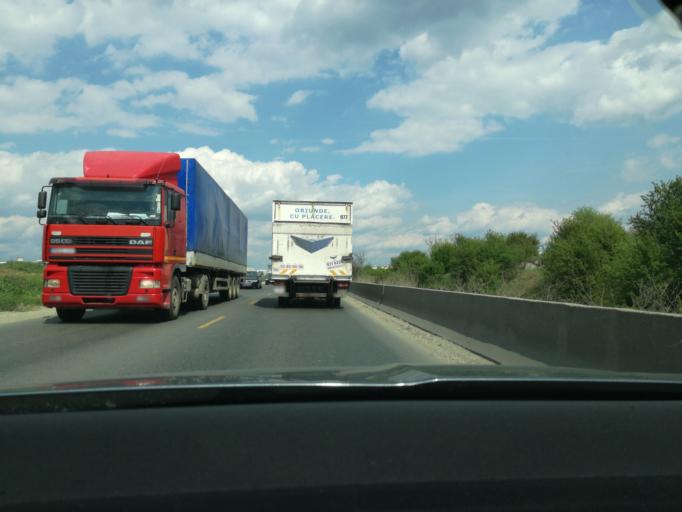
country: RO
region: Ilfov
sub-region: Comuna Chitila
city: Rudeni
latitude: 44.4761
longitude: 25.9669
